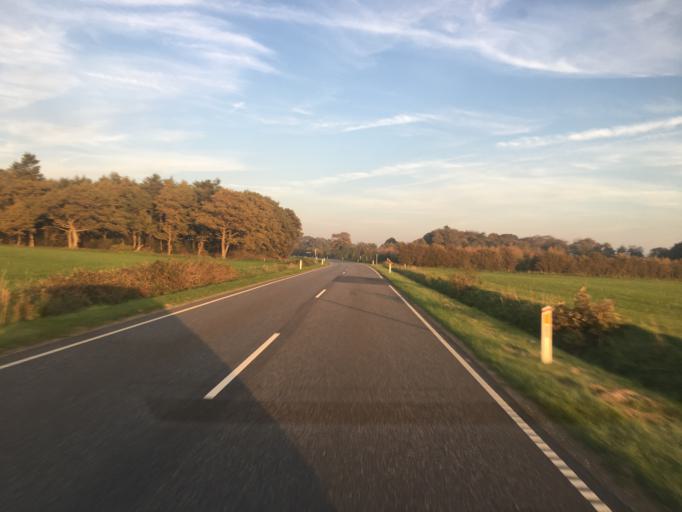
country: DK
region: South Denmark
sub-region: Tonder Kommune
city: Logumkloster
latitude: 55.0474
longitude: 9.0673
